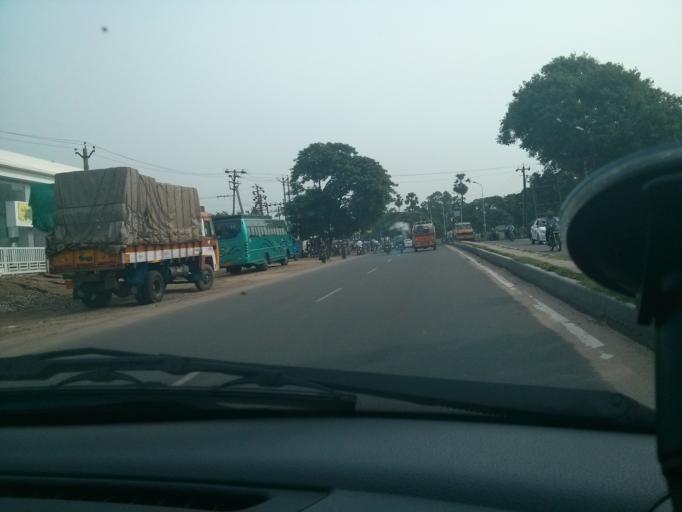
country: IN
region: Tamil Nadu
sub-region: Coimbatore
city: Coimbatore
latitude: 11.0352
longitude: 76.9507
